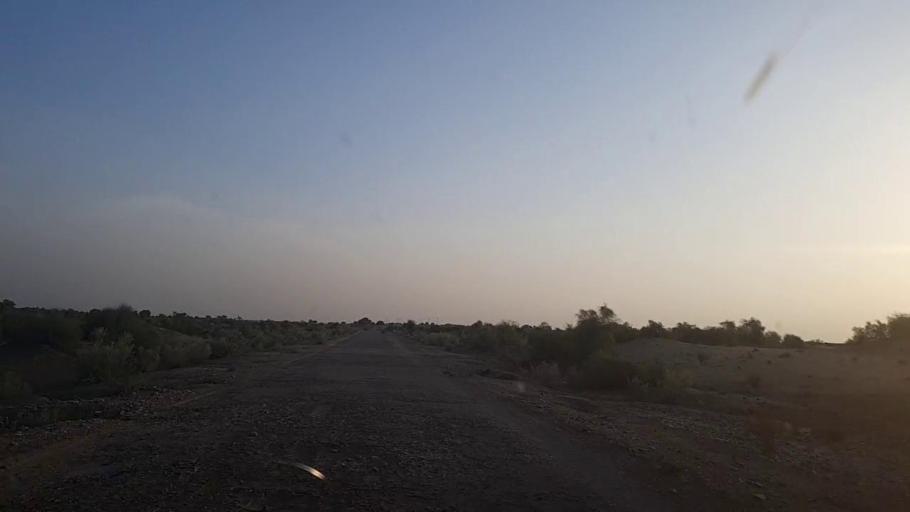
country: PK
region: Sindh
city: Khanpur
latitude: 27.6022
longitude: 69.4317
